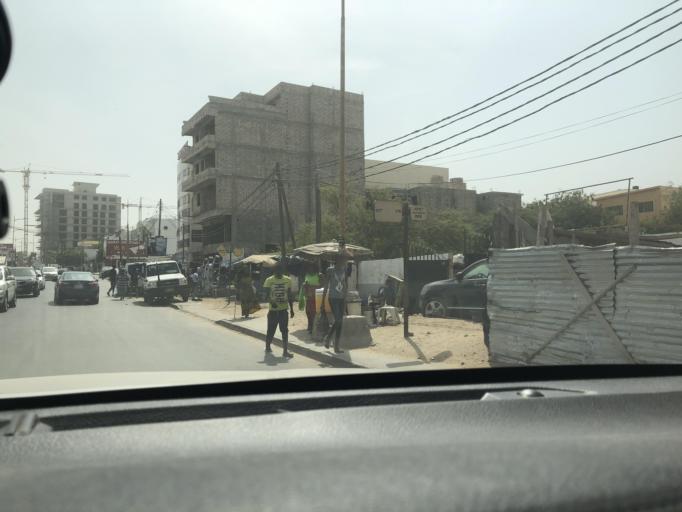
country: SN
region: Dakar
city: Mermoz Boabab
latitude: 14.7446
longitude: -17.5123
